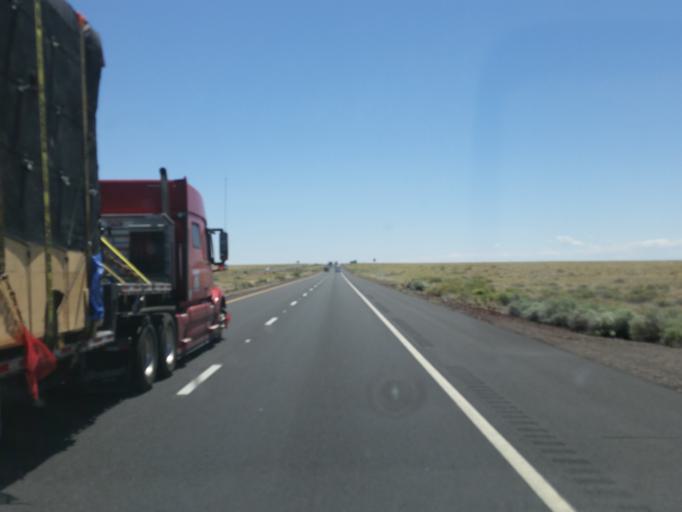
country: US
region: Arizona
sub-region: Coconino County
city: Flagstaff
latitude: 35.1384
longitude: -111.2097
